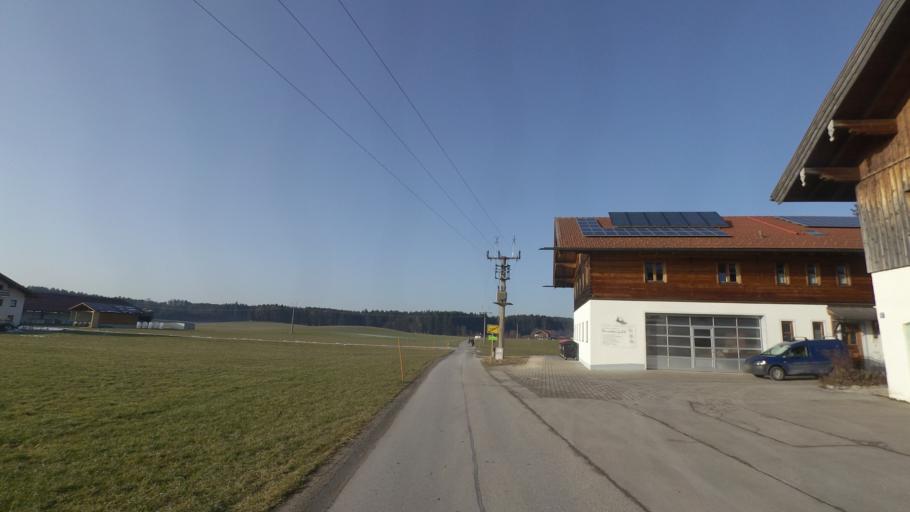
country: DE
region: Bavaria
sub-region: Upper Bavaria
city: Nussdorf
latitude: 47.9112
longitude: 12.5905
